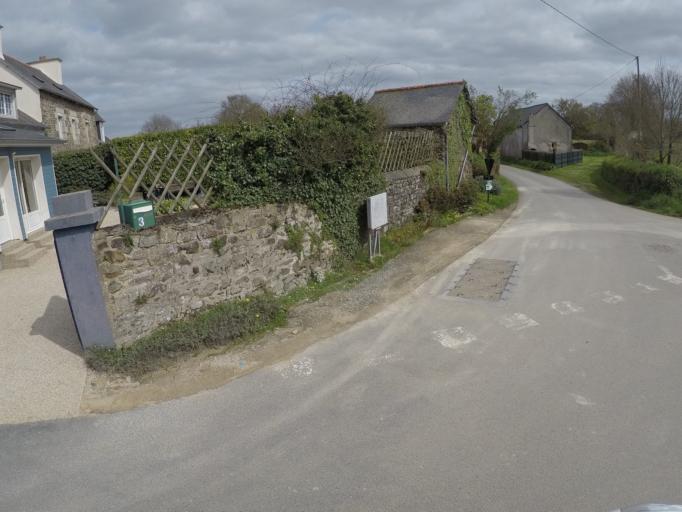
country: FR
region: Brittany
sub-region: Departement des Cotes-d'Armor
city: Plouezec
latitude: 48.7134
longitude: -2.9574
